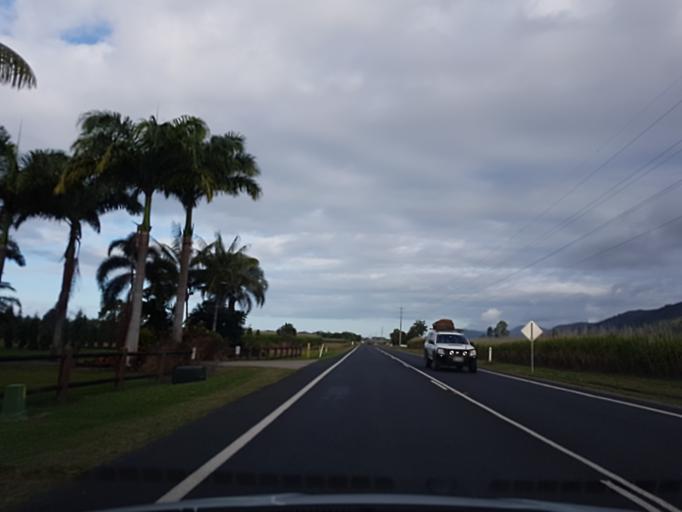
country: AU
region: Queensland
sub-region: Cairns
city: Port Douglas
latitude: -16.4937
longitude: 145.4237
